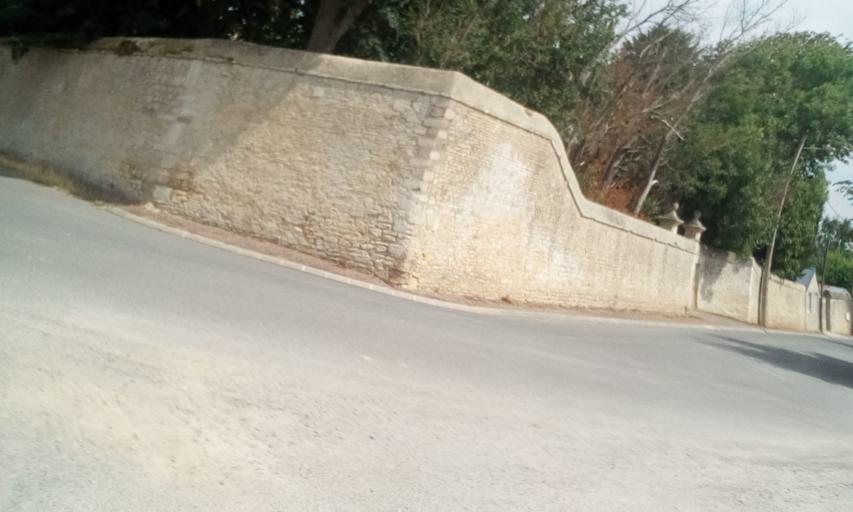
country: FR
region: Lower Normandy
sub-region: Departement du Calvados
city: Douvres-la-Delivrande
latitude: 49.2927
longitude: -0.3945
